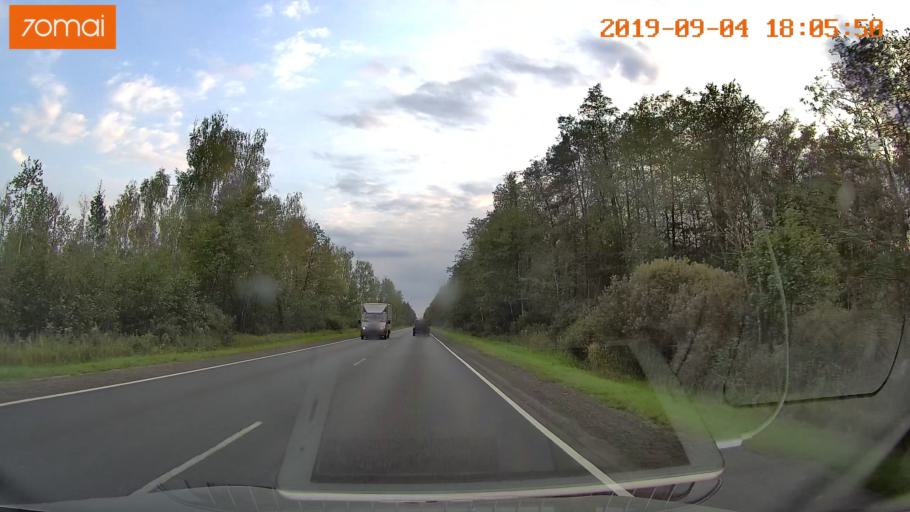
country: RU
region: Moskovskaya
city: Il'inskiy Pogost
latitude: 55.4371
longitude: 38.8217
